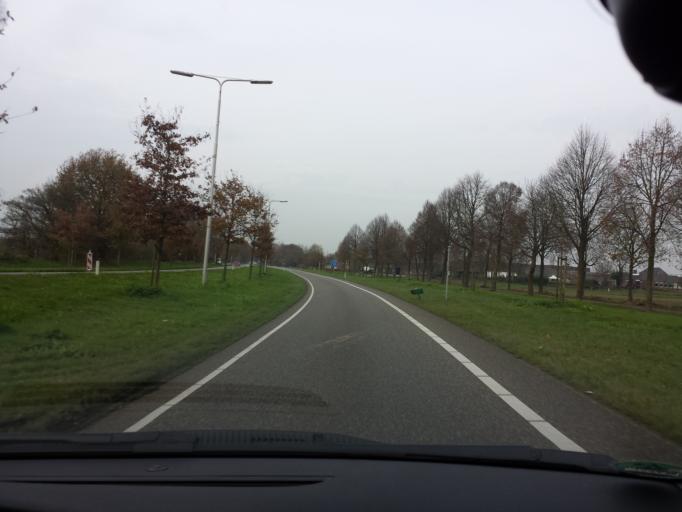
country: NL
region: Limburg
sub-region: Gemeente Gennep
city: Gennep
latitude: 51.7132
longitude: 5.9636
